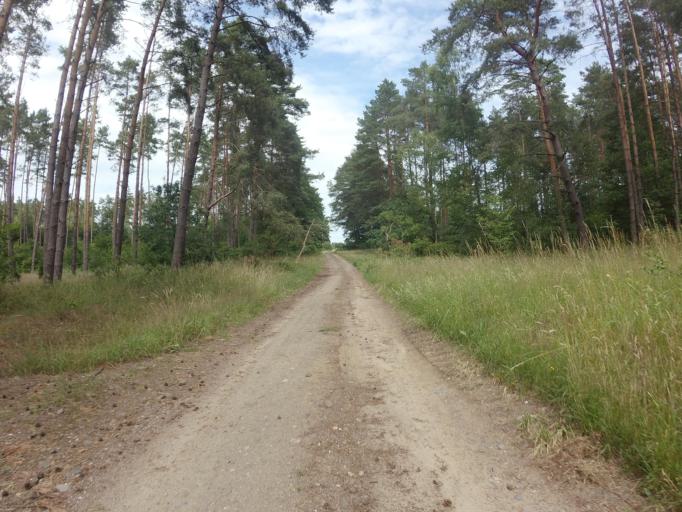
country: PL
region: Lubusz
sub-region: Powiat strzelecko-drezdenecki
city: Dobiegniew
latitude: 52.9947
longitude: 15.7256
